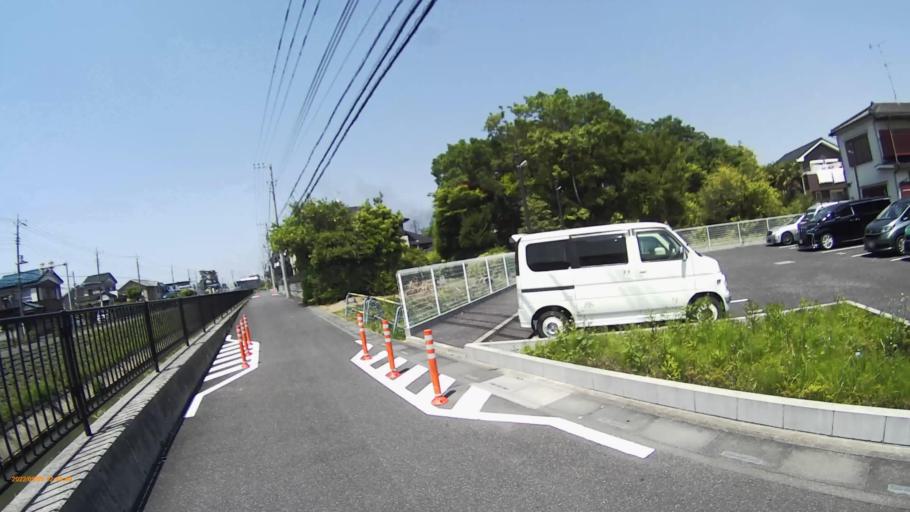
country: JP
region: Saitama
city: Kasukabe
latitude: 35.9425
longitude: 139.7766
